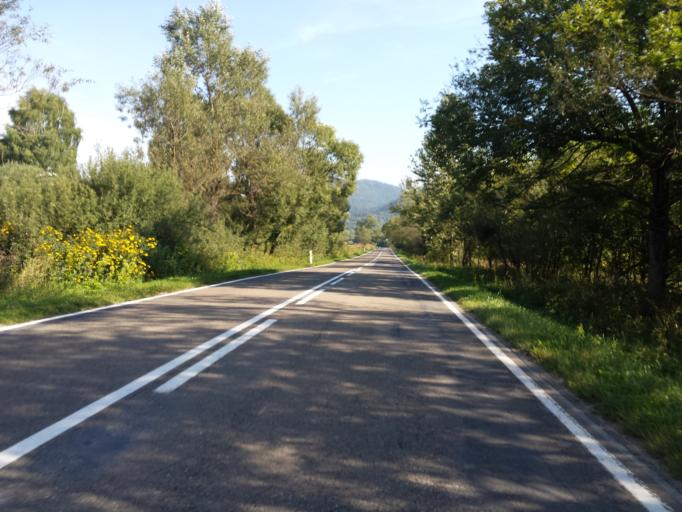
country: PL
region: Subcarpathian Voivodeship
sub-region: Powiat leski
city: Cisna
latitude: 49.2556
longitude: 22.2859
